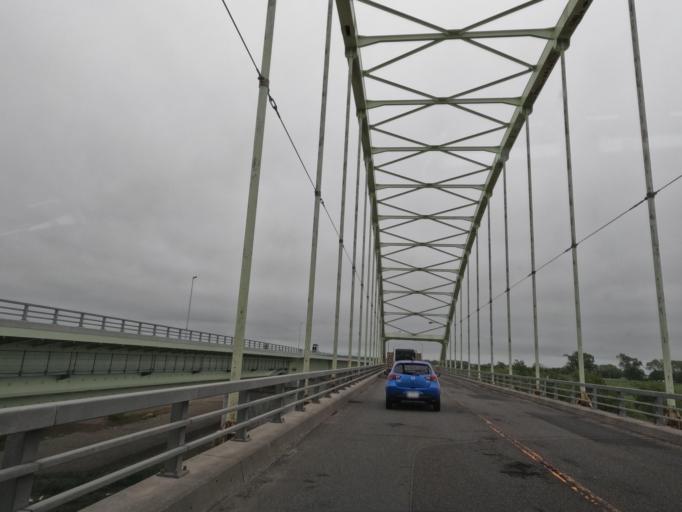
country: JP
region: Hokkaido
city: Ebetsu
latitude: 43.1362
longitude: 141.5120
